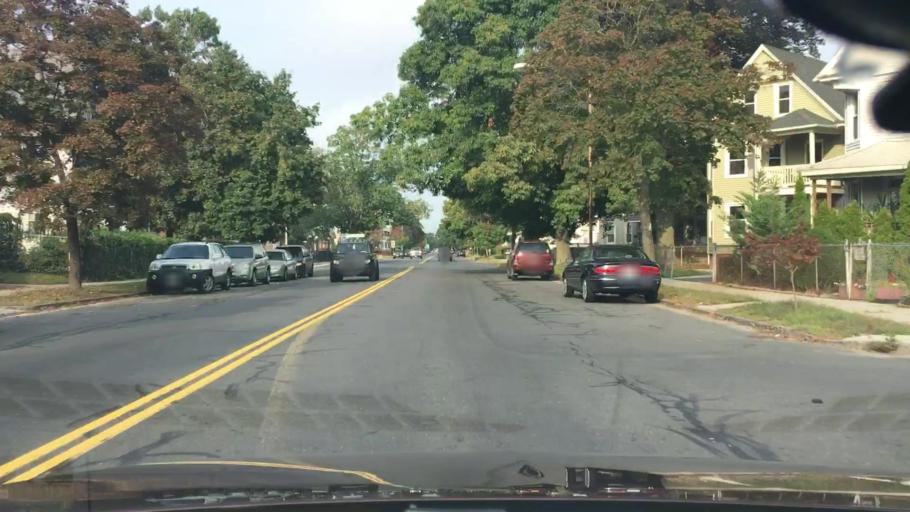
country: US
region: Massachusetts
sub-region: Hampden County
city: Springfield
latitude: 42.0852
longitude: -72.5519
